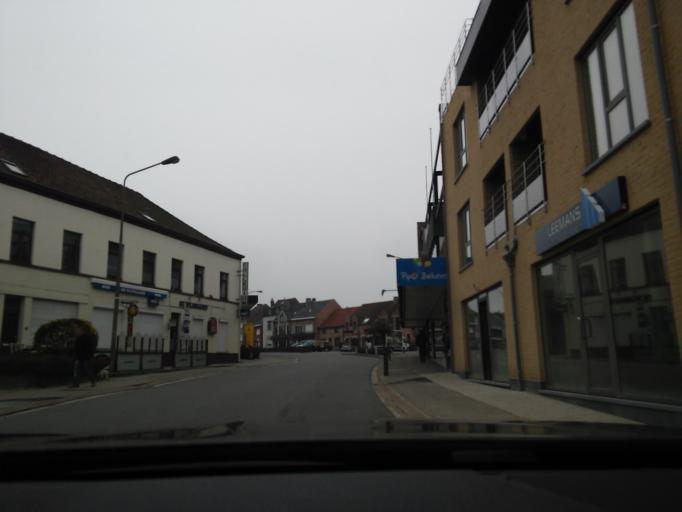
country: BE
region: Flanders
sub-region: Provincie Vlaams-Brabant
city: Dilbeek
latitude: 50.8712
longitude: 4.2622
